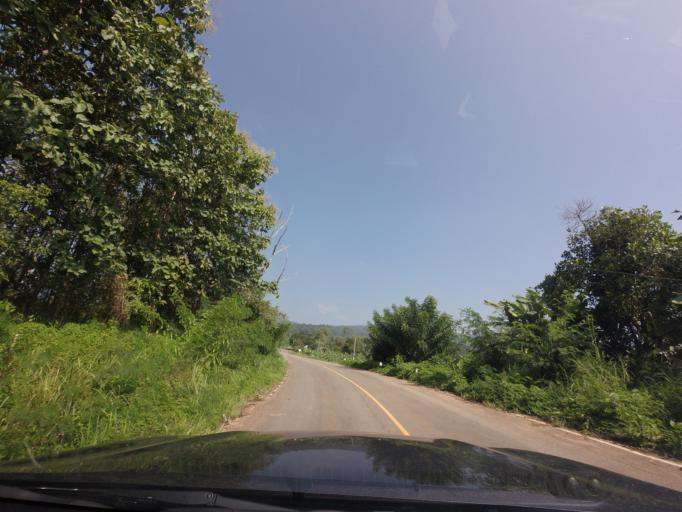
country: TH
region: Loei
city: Na Haeo
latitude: 17.4987
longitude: 101.0169
